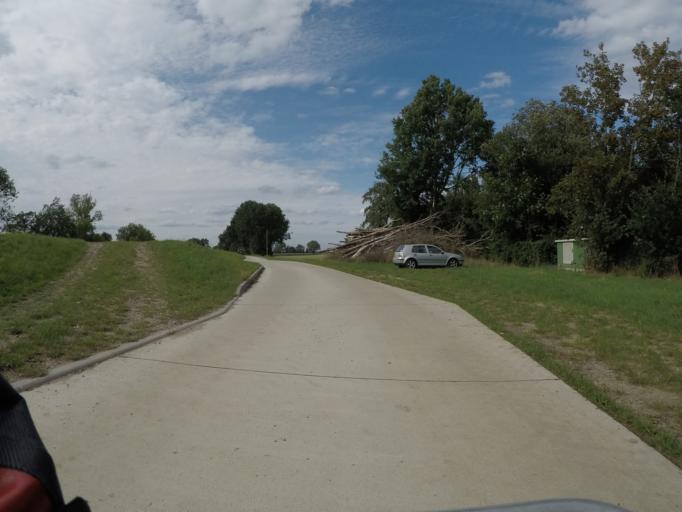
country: DE
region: Lower Saxony
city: Wittorf
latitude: 53.3468
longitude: 10.3836
